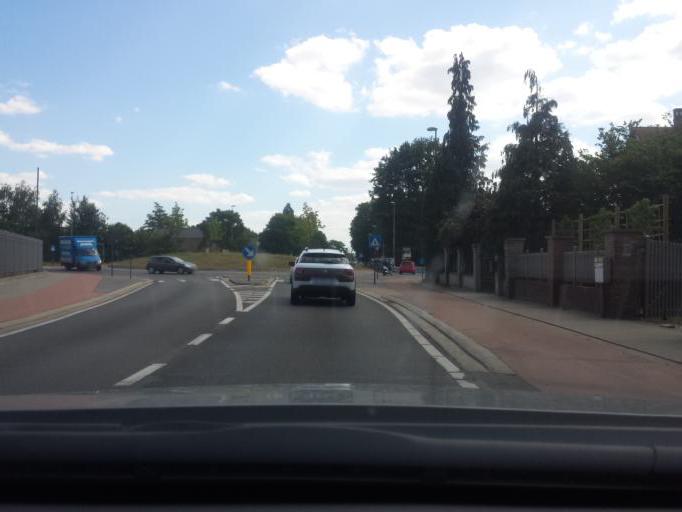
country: BE
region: Flanders
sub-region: Provincie Limburg
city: Beringen
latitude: 51.0647
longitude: 5.2216
